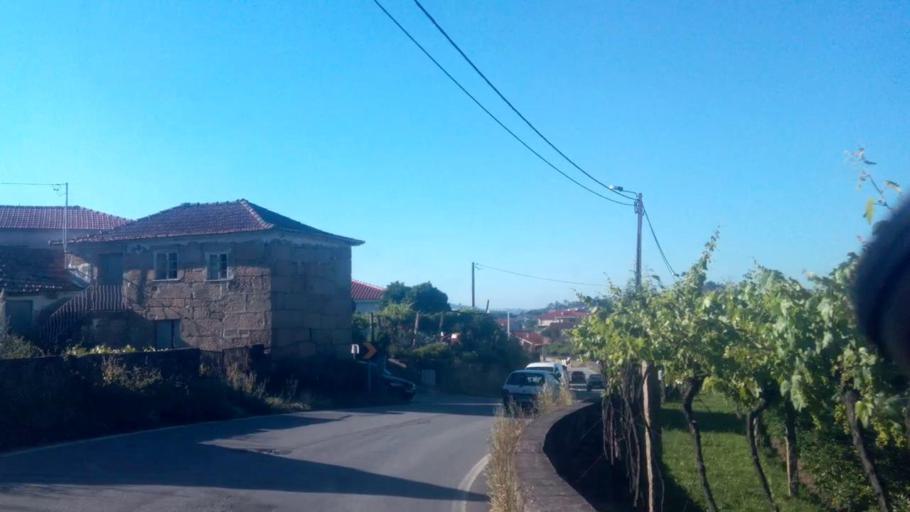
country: PT
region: Porto
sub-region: Penafiel
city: Penafiel
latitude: 41.1928
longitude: -8.2733
